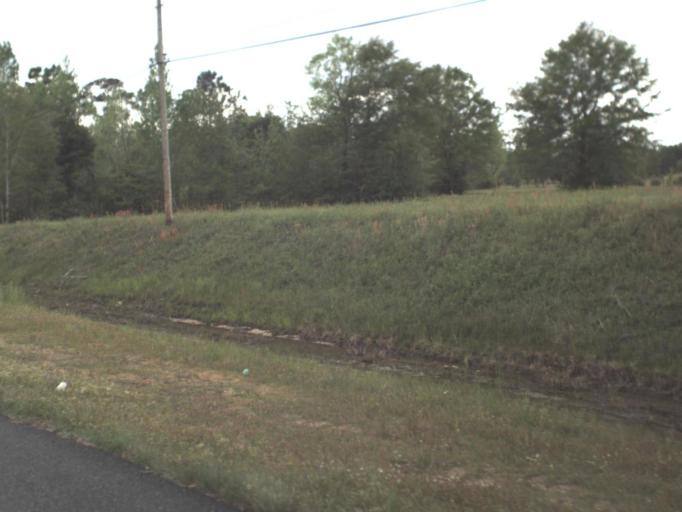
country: US
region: Florida
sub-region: Escambia County
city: Molino
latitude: 30.8459
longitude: -87.3229
